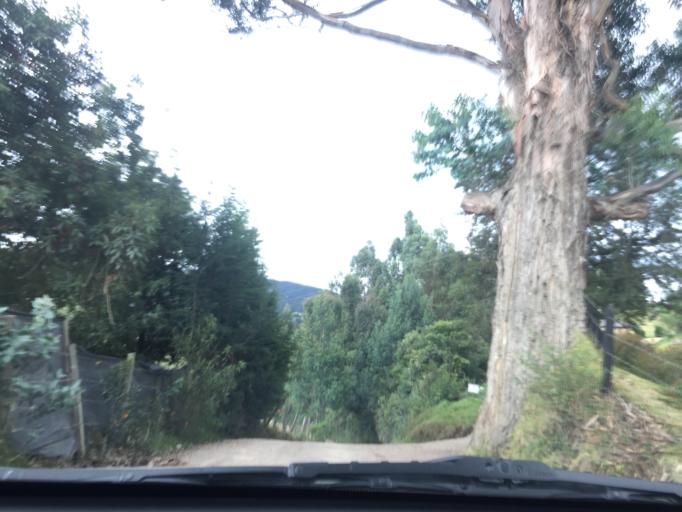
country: CO
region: Cundinamarca
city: Subachoque
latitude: 4.9397
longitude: -74.1461
